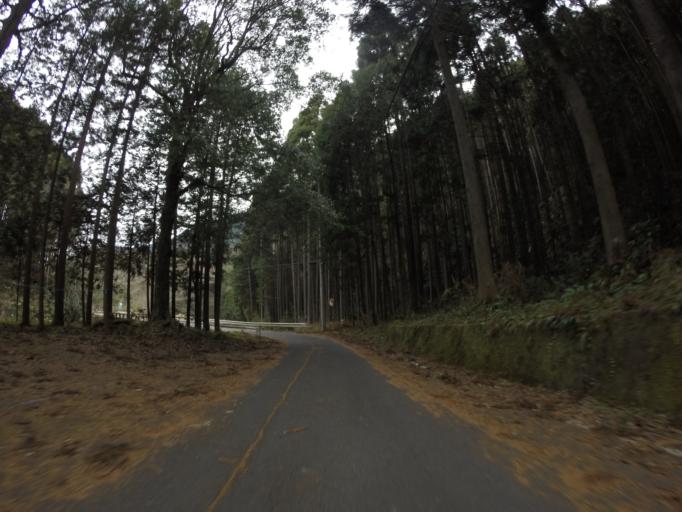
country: JP
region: Shizuoka
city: Fujinomiya
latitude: 35.2788
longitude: 138.5309
